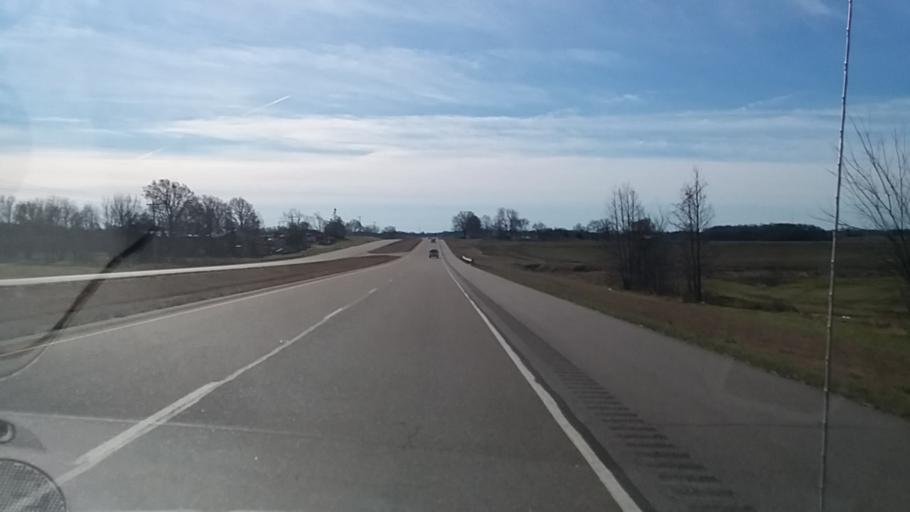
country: US
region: Tennessee
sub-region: Crockett County
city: Alamo
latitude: 35.8300
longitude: -89.1789
